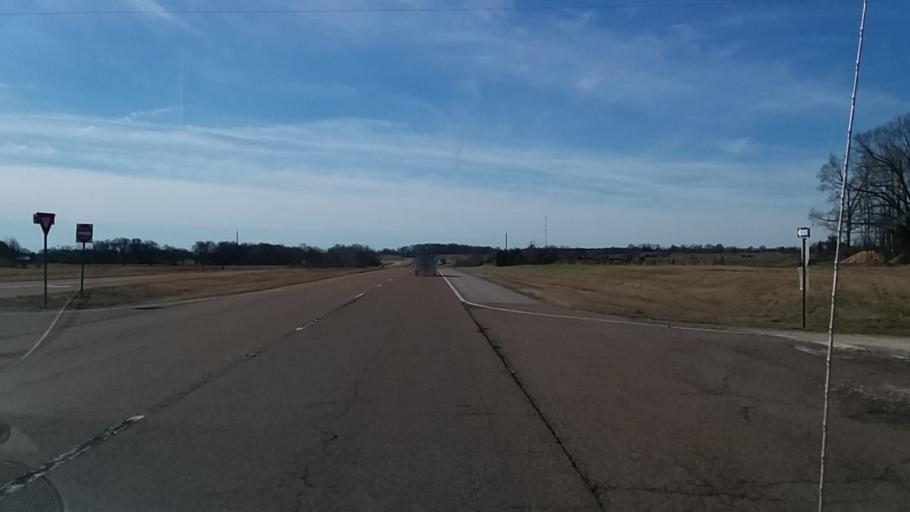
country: US
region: Tennessee
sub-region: Crockett County
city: Alamo
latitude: 35.8094
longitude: -89.1607
